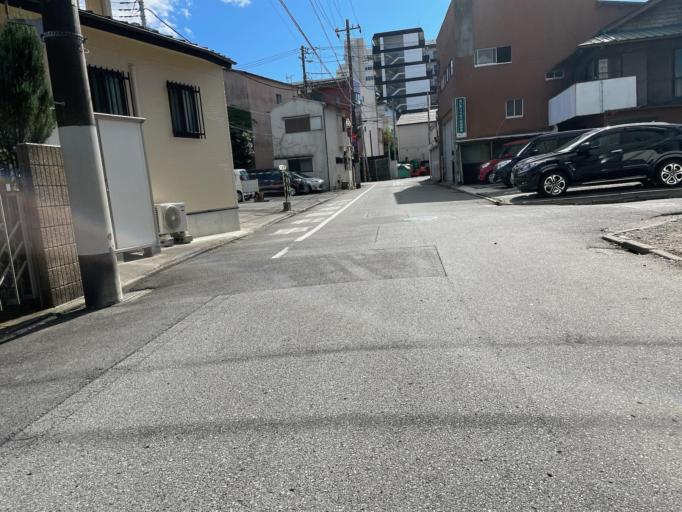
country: JP
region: Tochigi
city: Utsunomiya-shi
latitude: 36.5626
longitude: 139.8919
